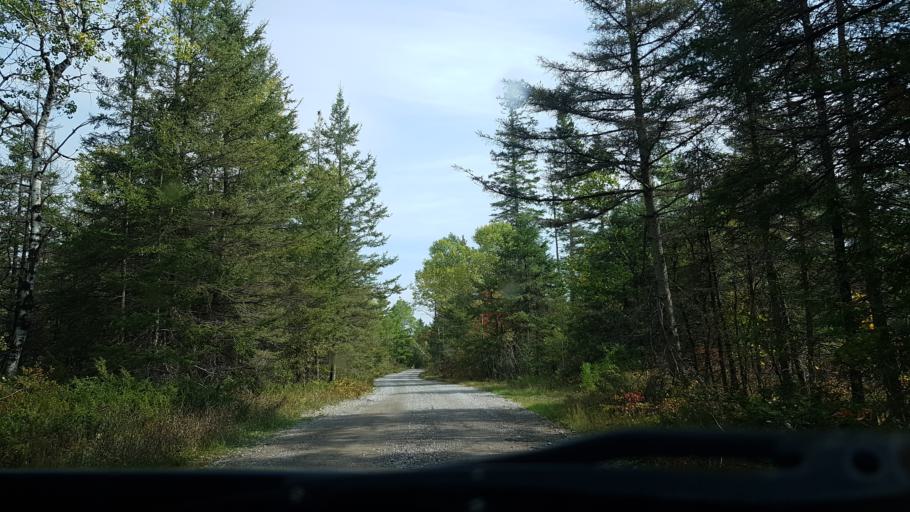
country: CA
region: Ontario
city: Orillia
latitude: 44.6782
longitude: -79.0785
